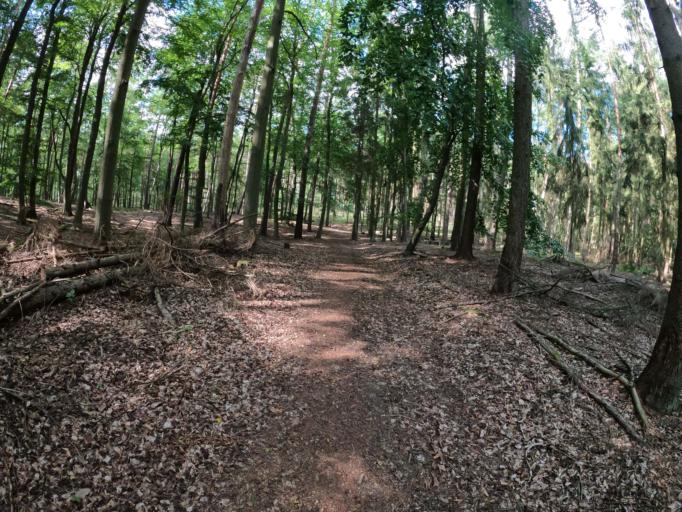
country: DE
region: Brandenburg
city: Angermunde
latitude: 53.0251
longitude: 13.9165
